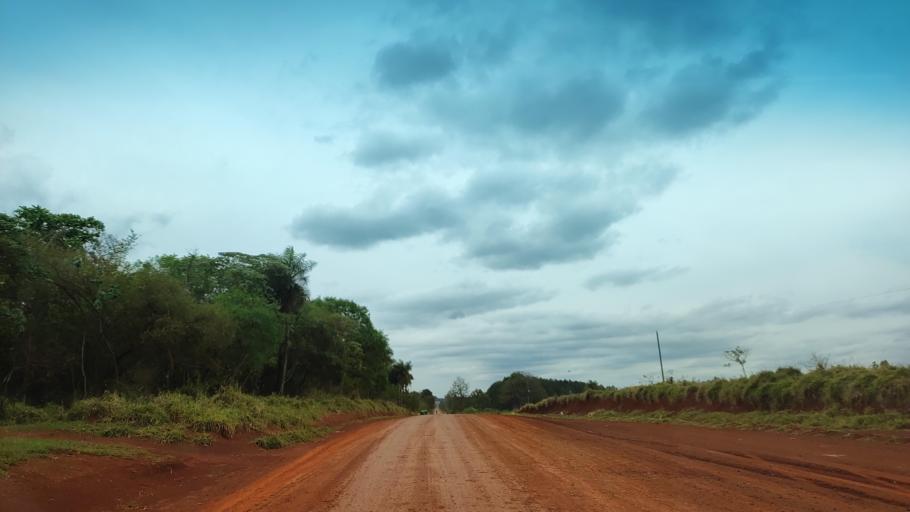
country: AR
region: Misiones
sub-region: Departamento de Capital
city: Posadas
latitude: -27.4868
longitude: -55.9708
